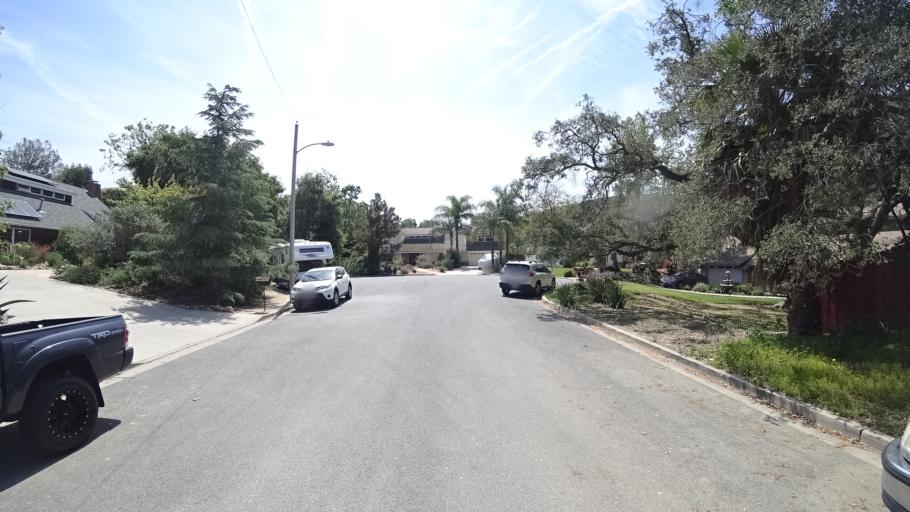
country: US
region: California
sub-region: Ventura County
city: Thousand Oaks
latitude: 34.2030
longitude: -118.8439
